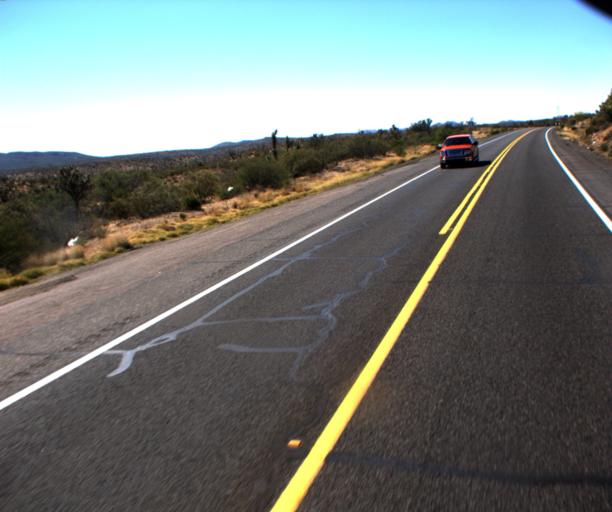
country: US
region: Arizona
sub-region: Yavapai County
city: Congress
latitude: 34.2307
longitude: -113.0706
